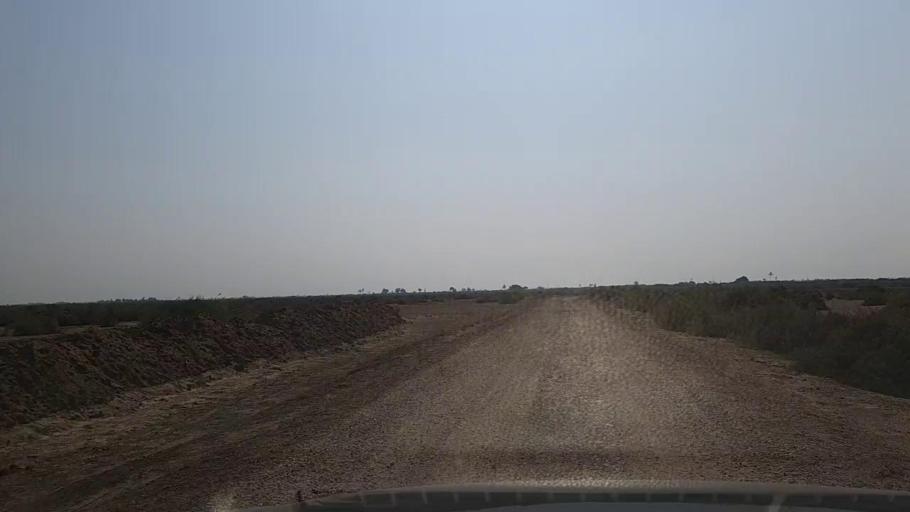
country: PK
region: Sindh
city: Mirpur Sakro
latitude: 24.4276
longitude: 67.7183
